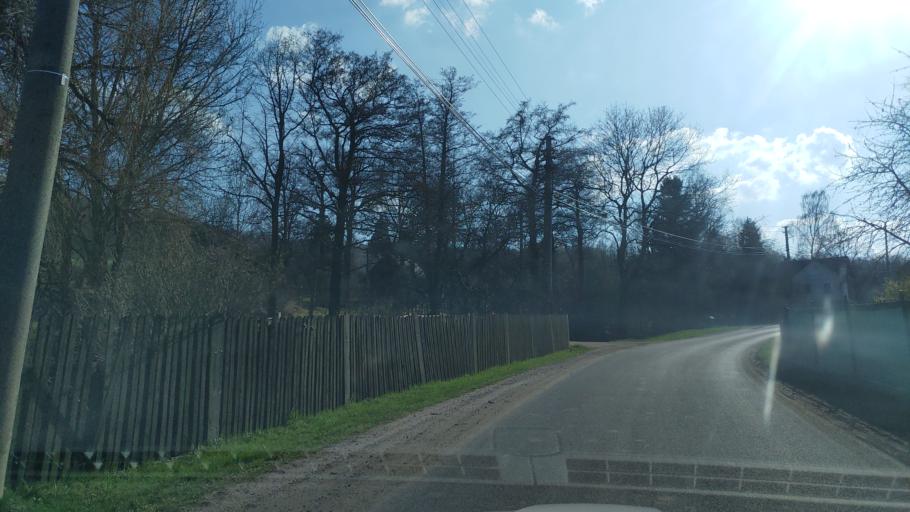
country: CZ
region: Ustecky
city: Vernerice
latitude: 50.6840
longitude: 14.3370
